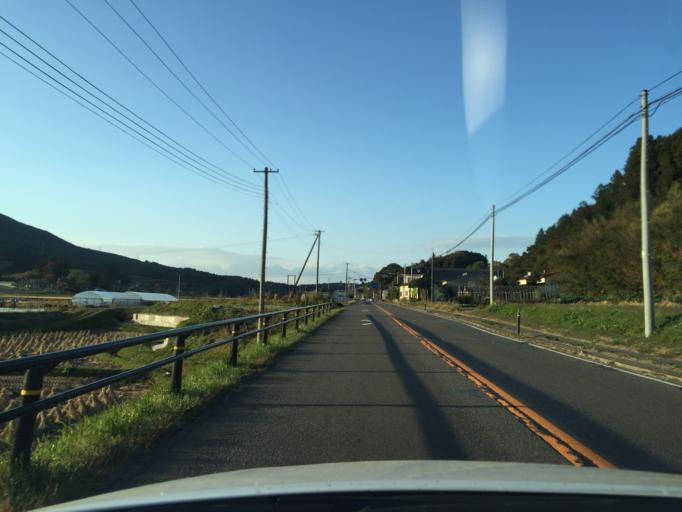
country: JP
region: Fukushima
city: Ishikawa
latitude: 37.2534
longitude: 140.5598
